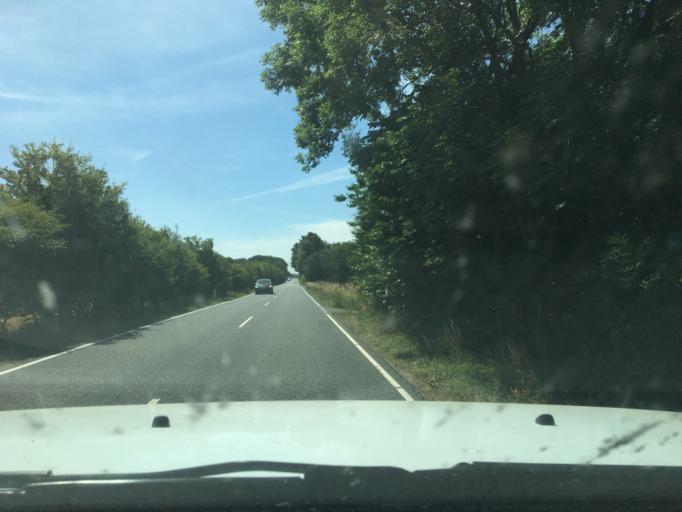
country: DK
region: Central Jutland
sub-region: Viborg Kommune
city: Bjerringbro
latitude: 56.5225
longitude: 9.6408
